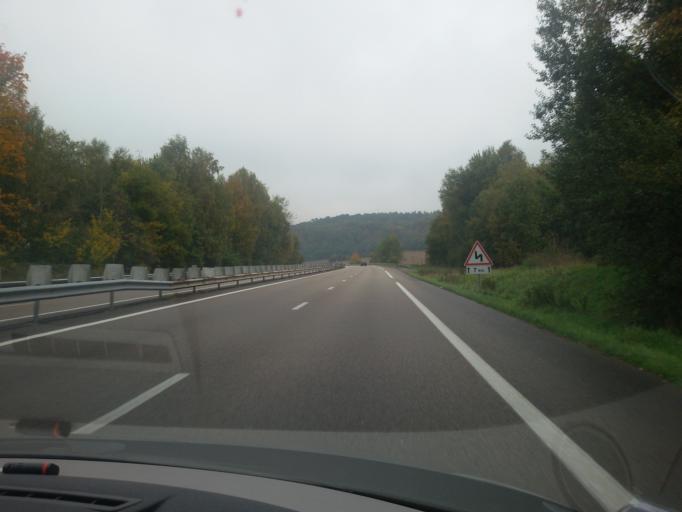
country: FR
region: Haute-Normandie
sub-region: Departement de l'Eure
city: Toutainville
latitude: 49.3530
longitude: 0.4516
